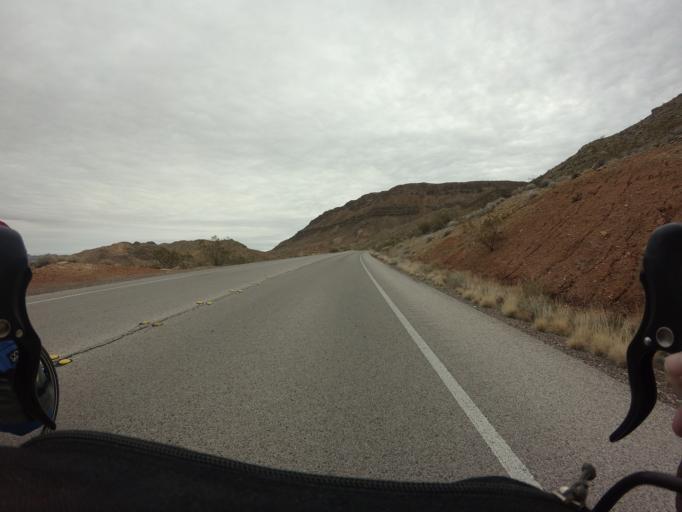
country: US
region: Nevada
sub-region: Clark County
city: Moapa Valley
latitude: 36.2327
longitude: -114.5704
